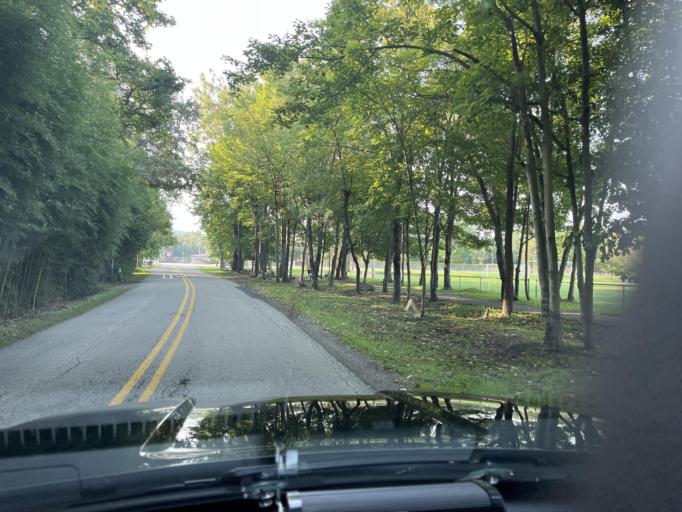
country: US
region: Pennsylvania
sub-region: Fayette County
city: Hopwood
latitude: 39.8668
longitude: -79.7137
